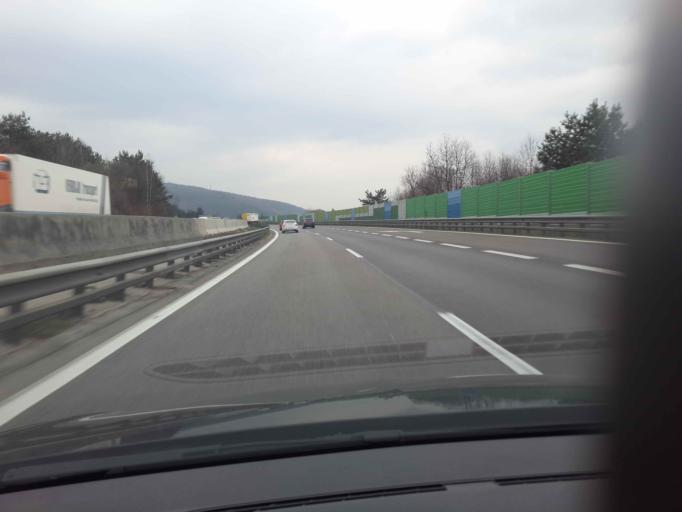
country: AT
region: Lower Austria
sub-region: Politischer Bezirk Modling
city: Gaaden
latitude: 48.0735
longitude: 16.1804
